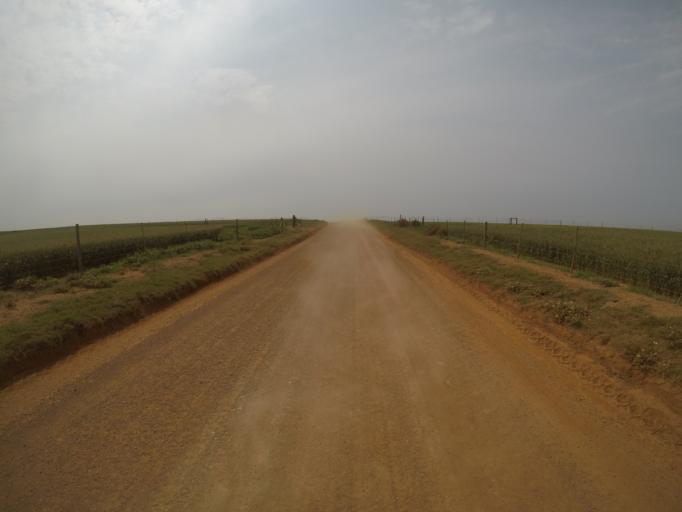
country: ZA
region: Western Cape
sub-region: City of Cape Town
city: Kraaifontein
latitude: -33.7219
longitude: 18.6741
